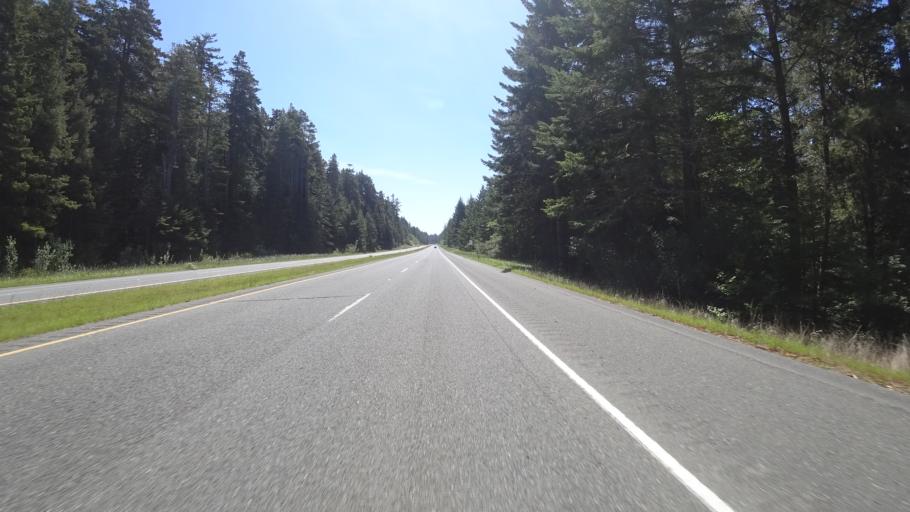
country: US
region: California
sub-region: Humboldt County
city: Westhaven-Moonstone
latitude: 41.0870
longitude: -124.1478
